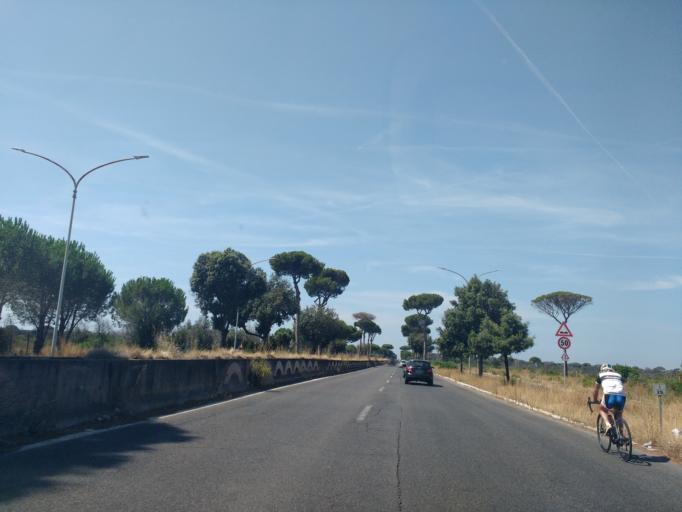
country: IT
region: Latium
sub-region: Citta metropolitana di Roma Capitale
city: Acilia-Castel Fusano-Ostia Antica
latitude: 41.7302
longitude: 12.3375
